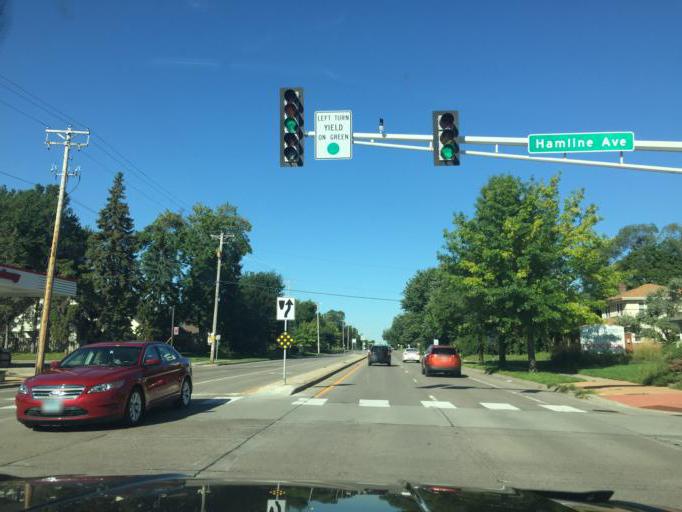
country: US
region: Minnesota
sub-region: Ramsey County
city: Falcon Heights
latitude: 44.9919
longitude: -93.1566
